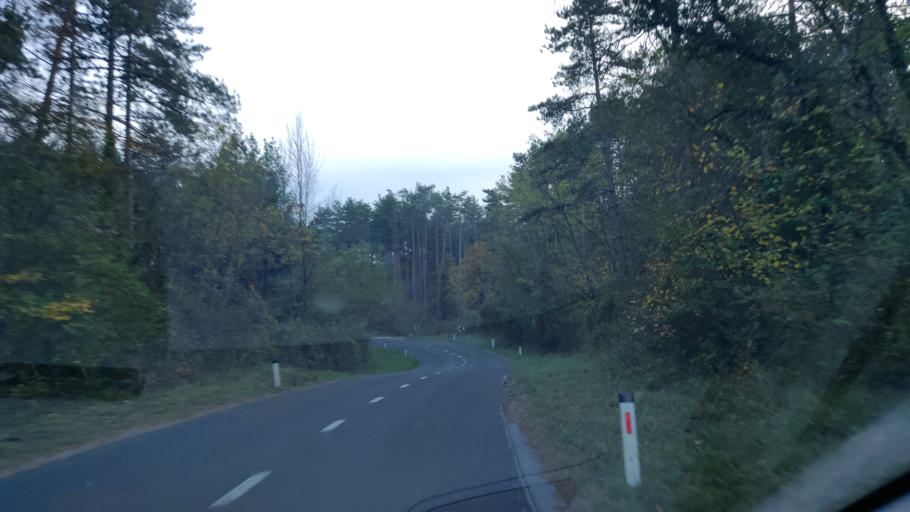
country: SI
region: Sezana
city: Sezana
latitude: 45.7703
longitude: 13.8794
